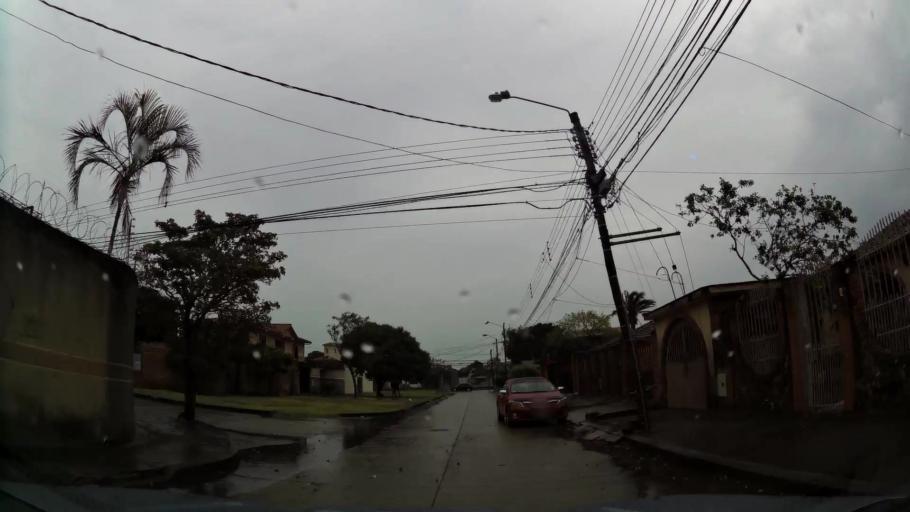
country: BO
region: Santa Cruz
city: Santa Cruz de la Sierra
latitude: -17.7714
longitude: -63.1496
